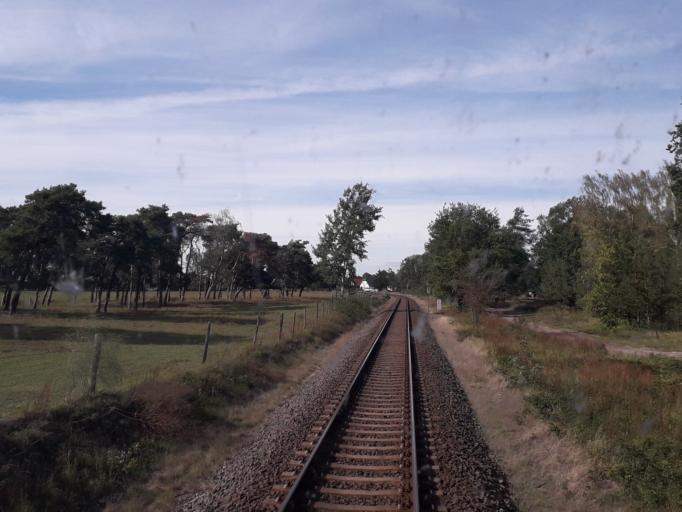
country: DE
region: Brandenburg
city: Kremmen
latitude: 52.7998
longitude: 13.0294
